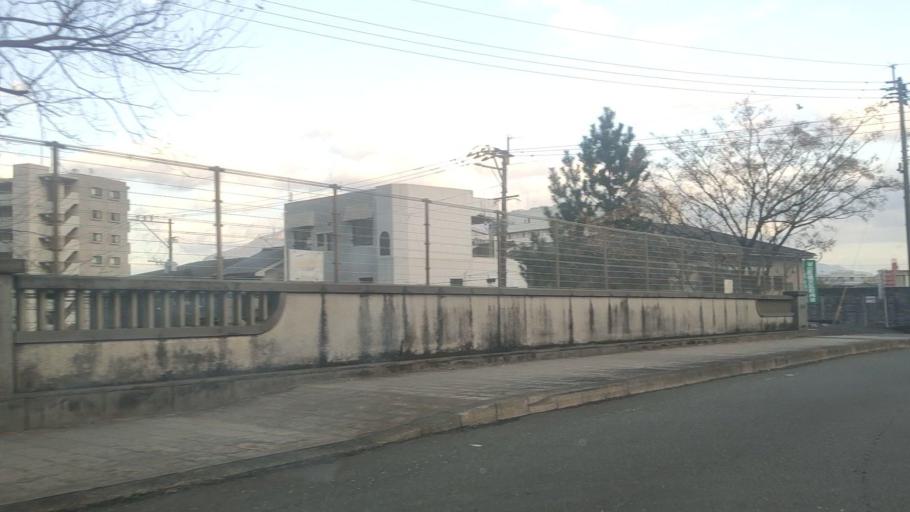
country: JP
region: Kagoshima
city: Kagoshima-shi
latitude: 31.6008
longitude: 130.5543
